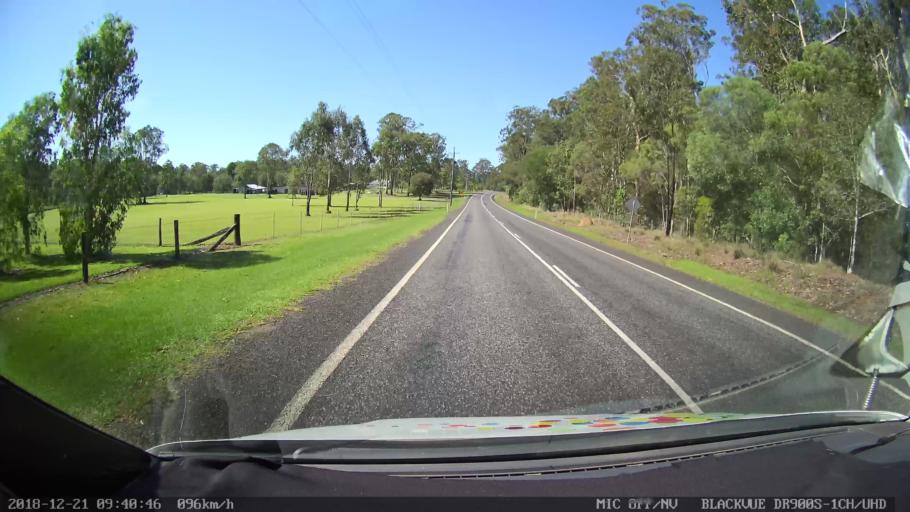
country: AU
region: New South Wales
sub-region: Clarence Valley
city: Grafton
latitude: -29.5773
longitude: 152.9624
